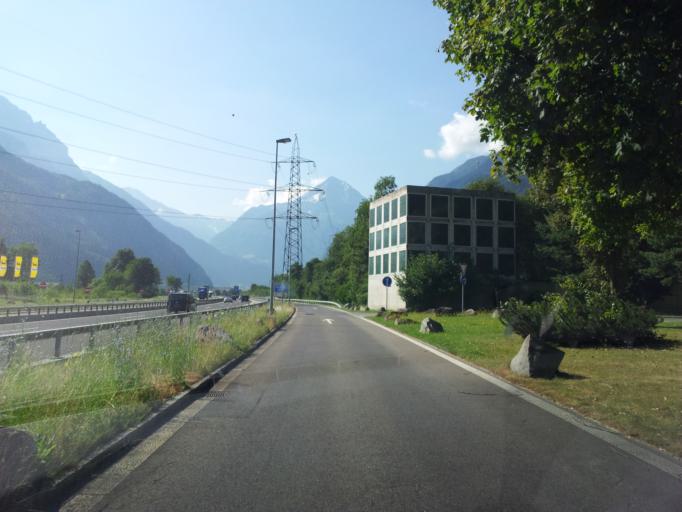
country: CH
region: Uri
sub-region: Uri
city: Attinghausen
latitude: 46.8465
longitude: 8.6329
